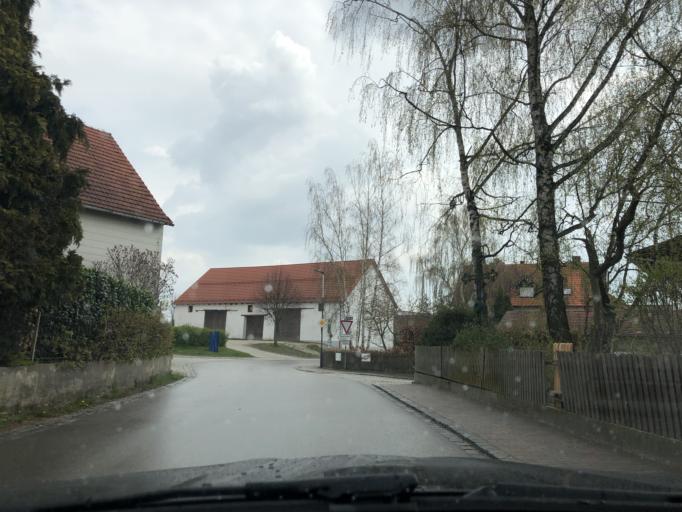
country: DE
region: Bavaria
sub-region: Upper Bavaria
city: Wolfersdorf
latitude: 48.4809
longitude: 11.7071
